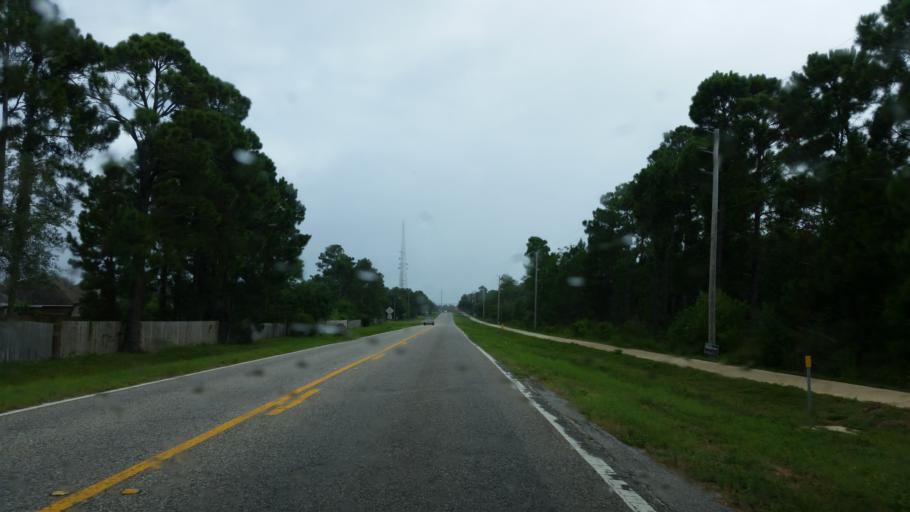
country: US
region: Florida
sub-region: Santa Rosa County
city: Woodlawn Beach
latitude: 30.4075
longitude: -86.9998
